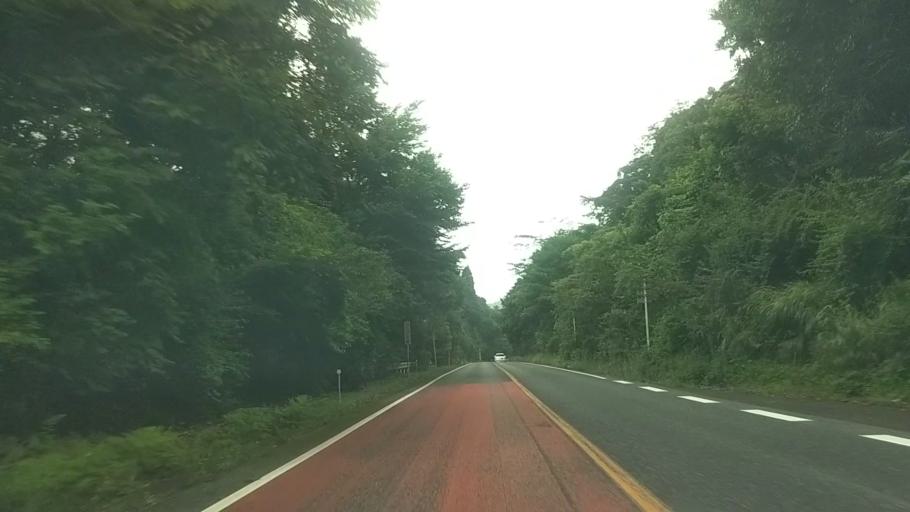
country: JP
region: Chiba
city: Kawaguchi
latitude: 35.2166
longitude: 140.0423
